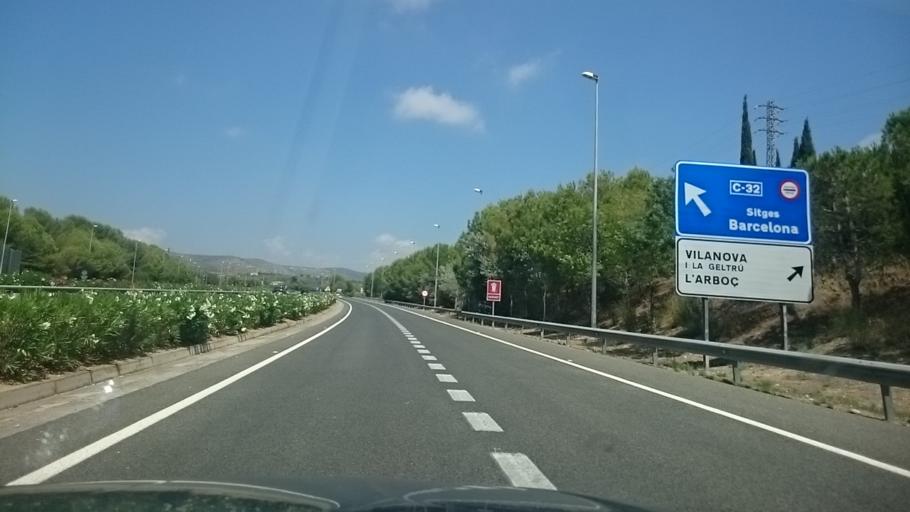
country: ES
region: Catalonia
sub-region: Provincia de Barcelona
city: Cubelles
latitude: 41.2237
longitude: 1.6772
